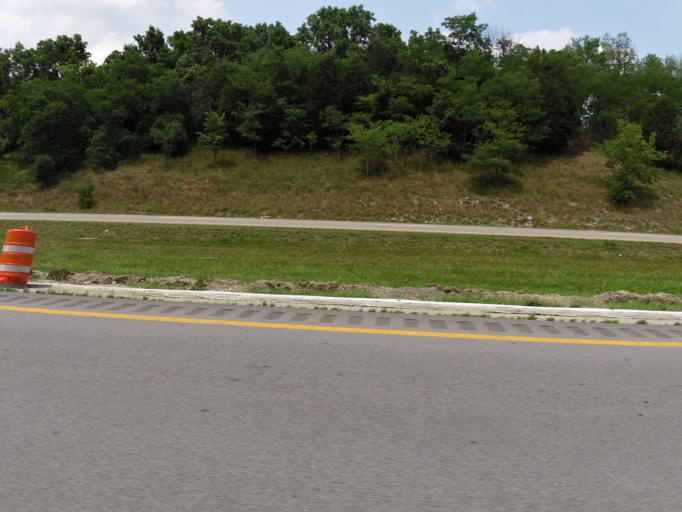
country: US
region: Kentucky
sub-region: Carroll County
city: Carrollton
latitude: 38.6535
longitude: -85.1034
